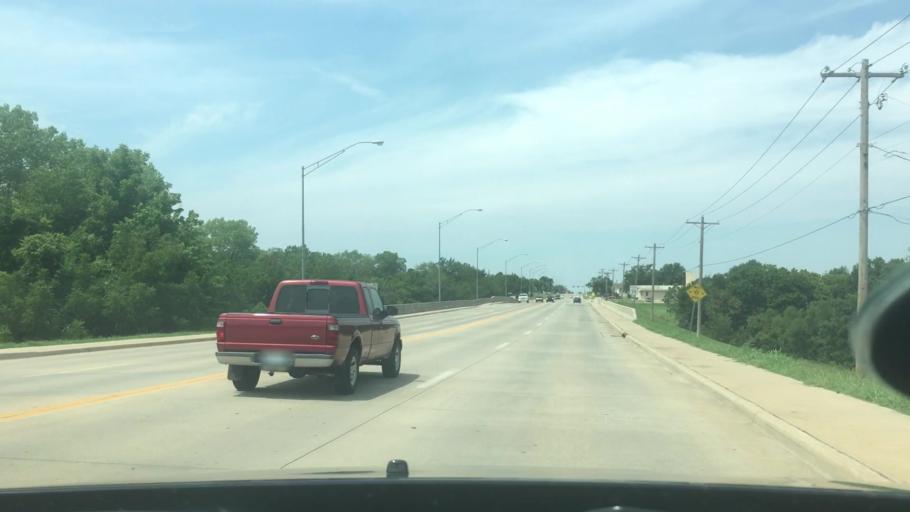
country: US
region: Oklahoma
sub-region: Pottawatomie County
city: Shawnee
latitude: 35.3617
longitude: -96.9140
